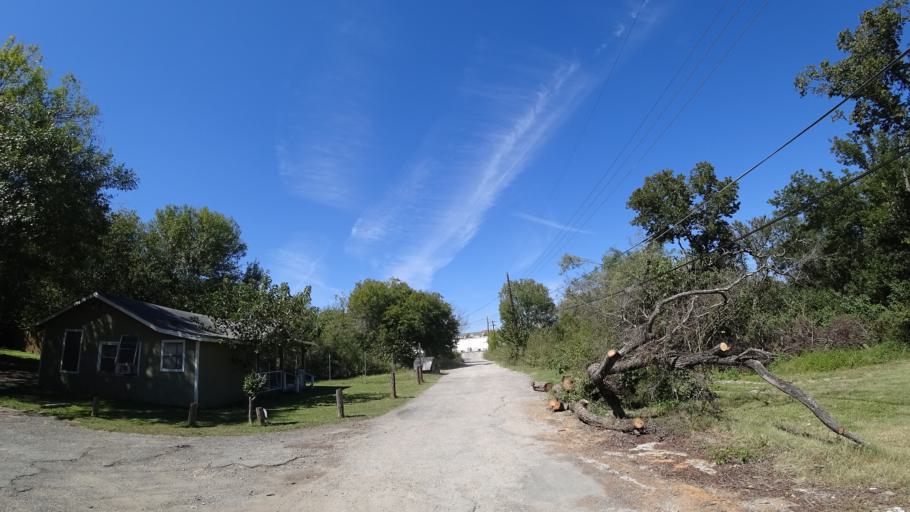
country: US
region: Texas
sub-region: Travis County
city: Austin
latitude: 30.2138
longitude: -97.6871
